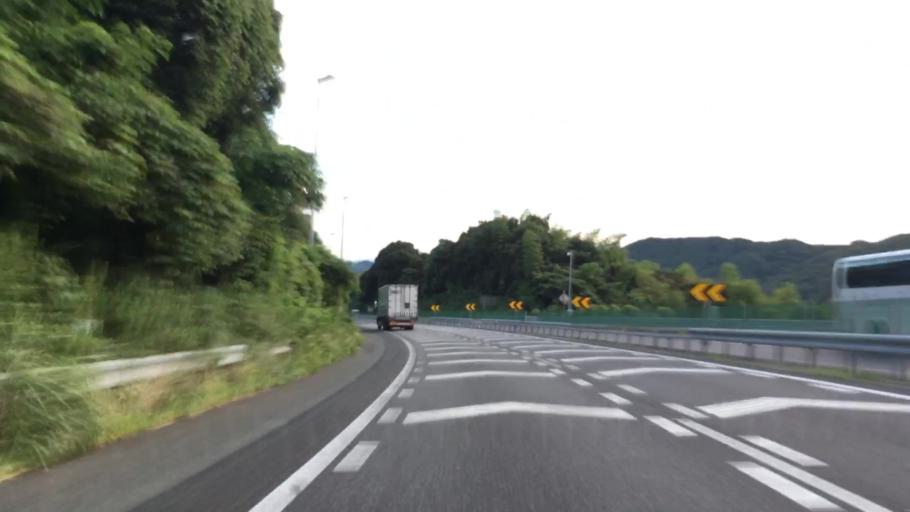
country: JP
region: Yamaguchi
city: Shimonoseki
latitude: 34.0344
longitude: 130.9632
